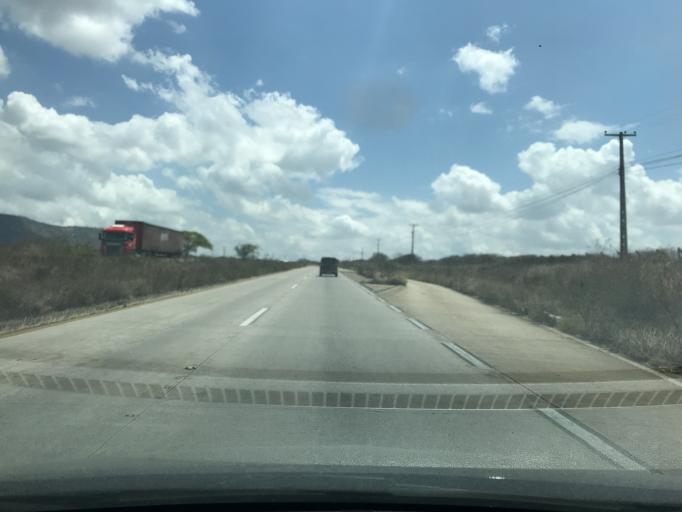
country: BR
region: Pernambuco
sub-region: Bezerros
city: Bezerros
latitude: -8.2920
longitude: -35.8238
